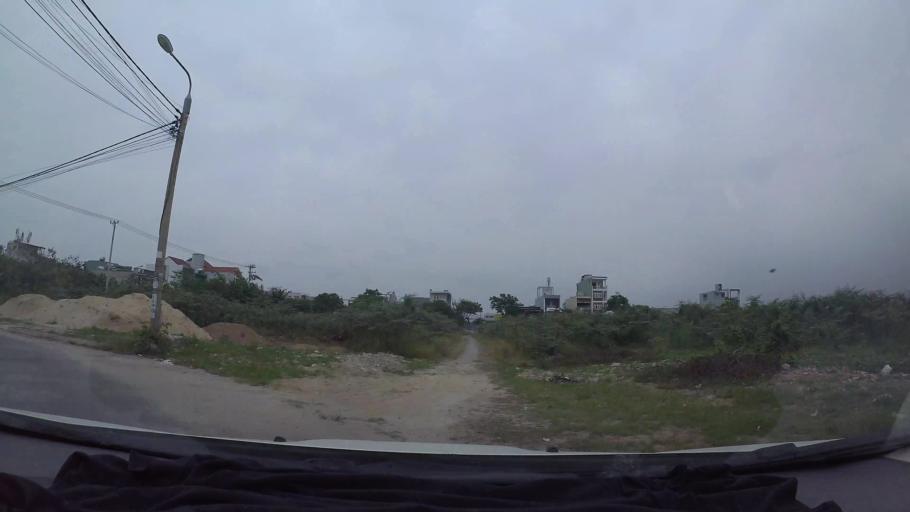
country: VN
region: Da Nang
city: Lien Chieu
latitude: 16.0769
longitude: 108.1586
